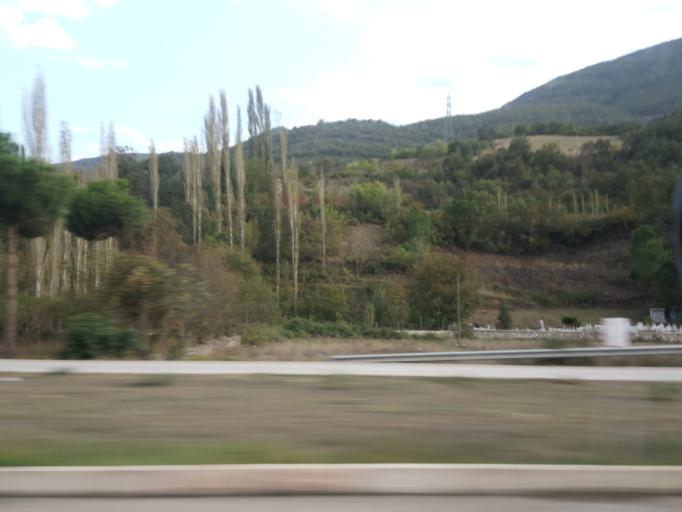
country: TR
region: Tokat
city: Basciftlik
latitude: 40.4182
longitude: 37.1944
